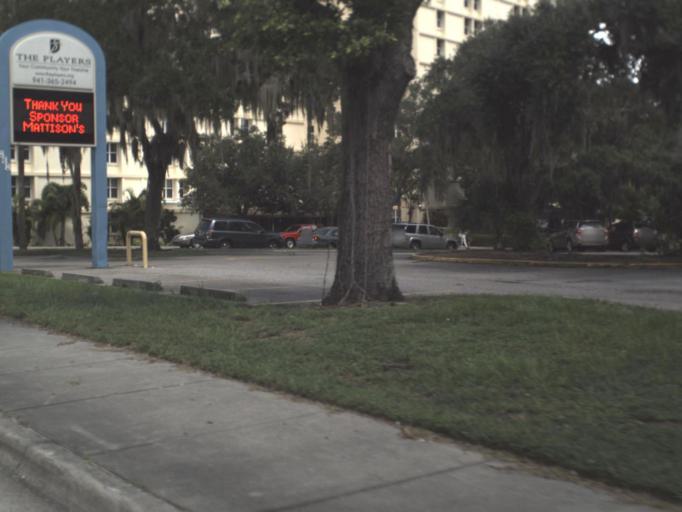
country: US
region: Florida
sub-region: Sarasota County
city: Sarasota
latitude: 27.3436
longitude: -82.5467
